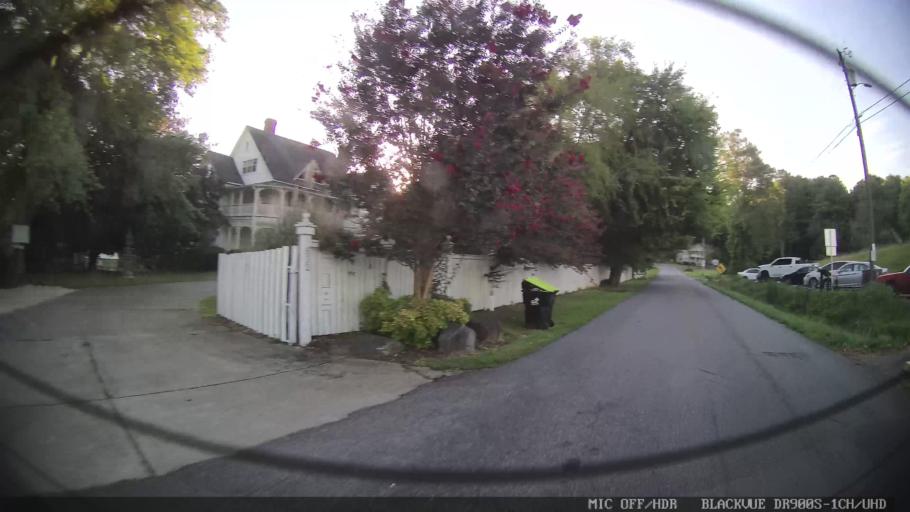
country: US
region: Georgia
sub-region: Bartow County
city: Emerson
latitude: 34.1138
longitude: -84.7152
